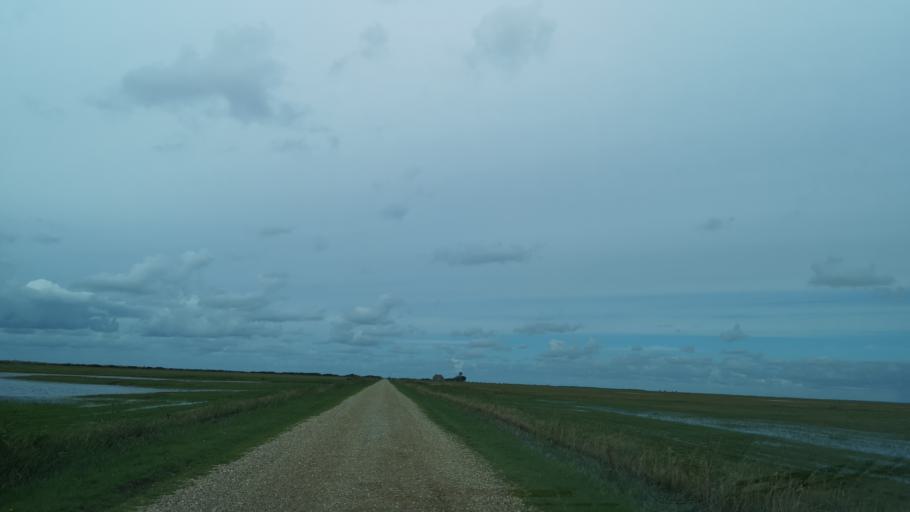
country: DK
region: Central Jutland
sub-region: Ringkobing-Skjern Kommune
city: Hvide Sande
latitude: 55.8870
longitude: 8.2188
